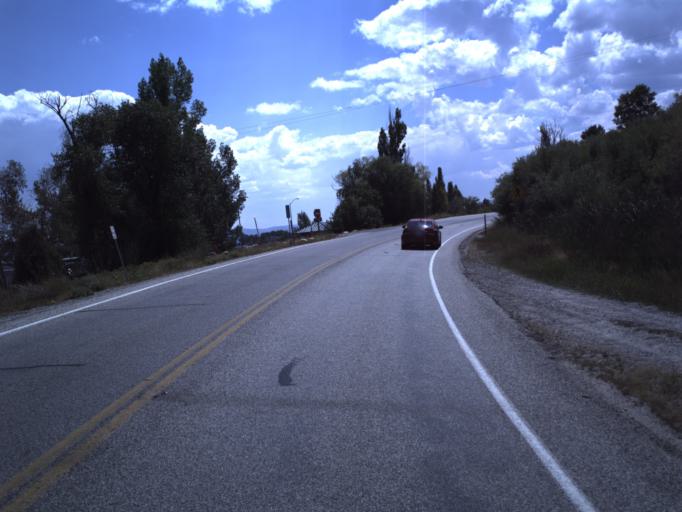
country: US
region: Idaho
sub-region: Bear Lake County
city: Paris
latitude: 41.9669
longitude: -111.3996
